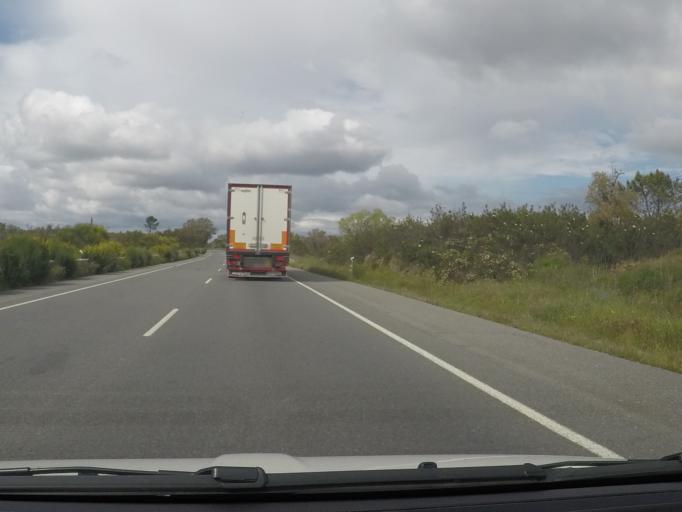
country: PT
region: Setubal
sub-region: Grandola
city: Grandola
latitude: 38.1447
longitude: -8.6507
